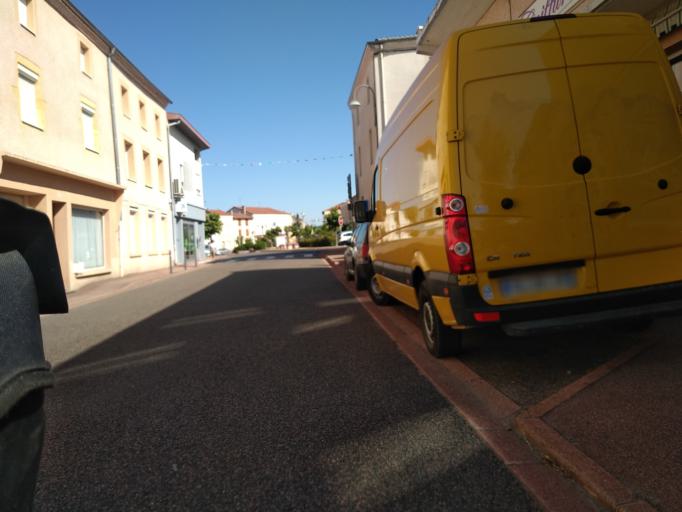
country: FR
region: Rhone-Alpes
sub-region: Departement de la Loire
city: Neulise
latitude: 45.9019
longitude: 4.1809
